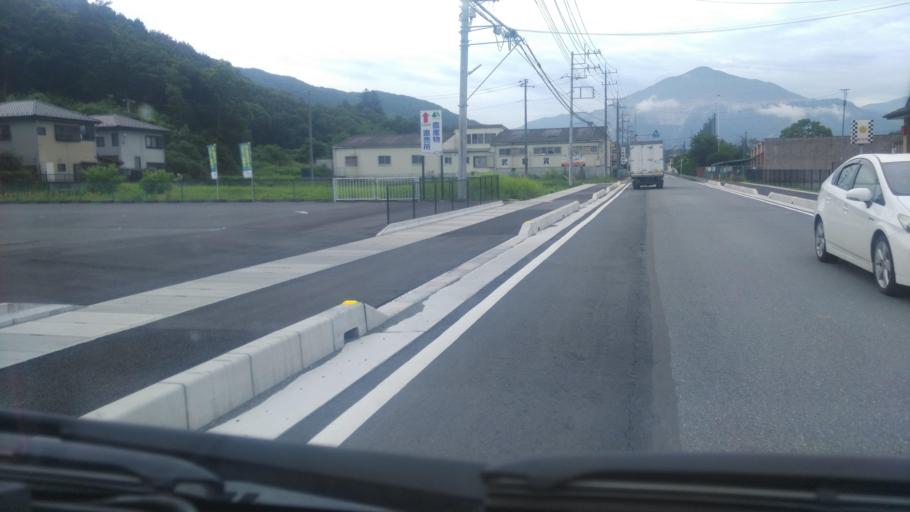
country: JP
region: Saitama
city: Chichibu
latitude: 36.0196
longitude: 139.1130
